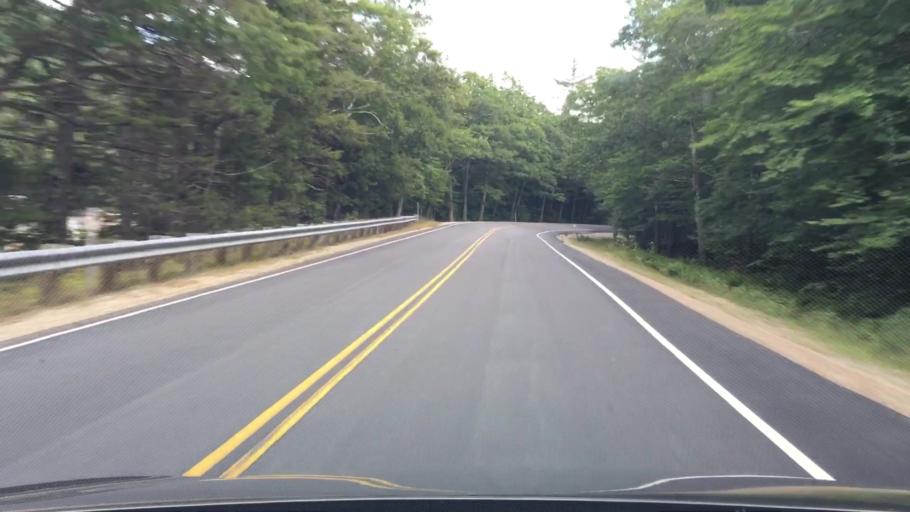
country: US
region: New Hampshire
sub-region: Carroll County
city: Conway
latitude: 43.9986
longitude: -71.2279
